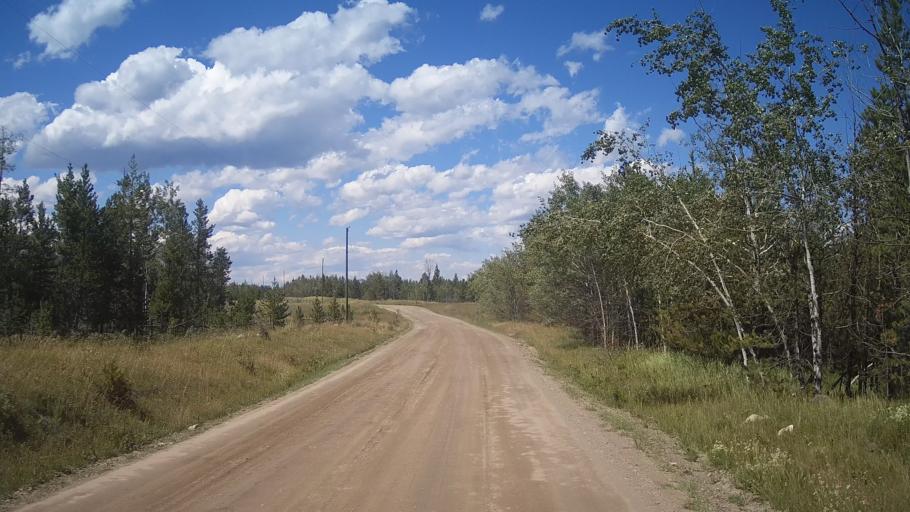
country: CA
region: British Columbia
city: Cache Creek
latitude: 51.2661
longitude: -121.7004
